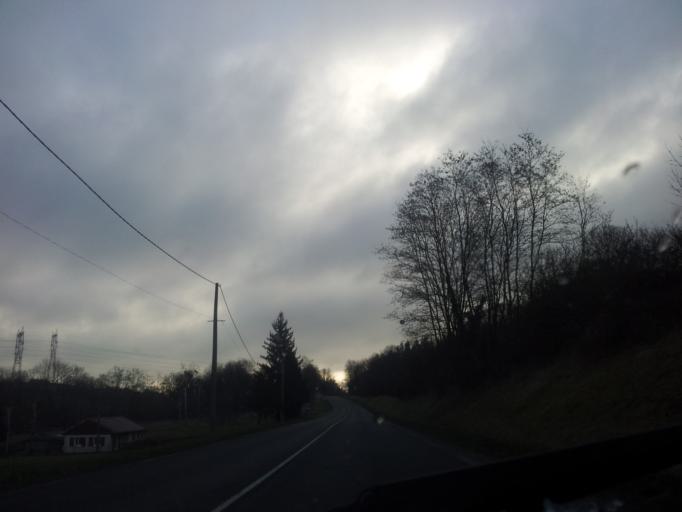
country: FR
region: Auvergne
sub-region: Departement de l'Allier
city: Saint-Pourcain-sur-Sioule
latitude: 46.3178
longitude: 3.2465
